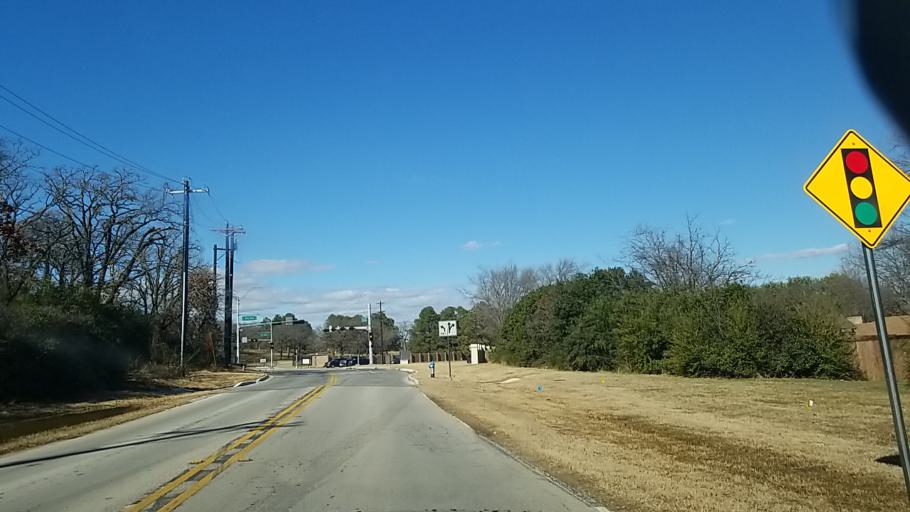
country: US
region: Texas
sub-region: Denton County
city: Corinth
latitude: 33.1642
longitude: -97.0901
